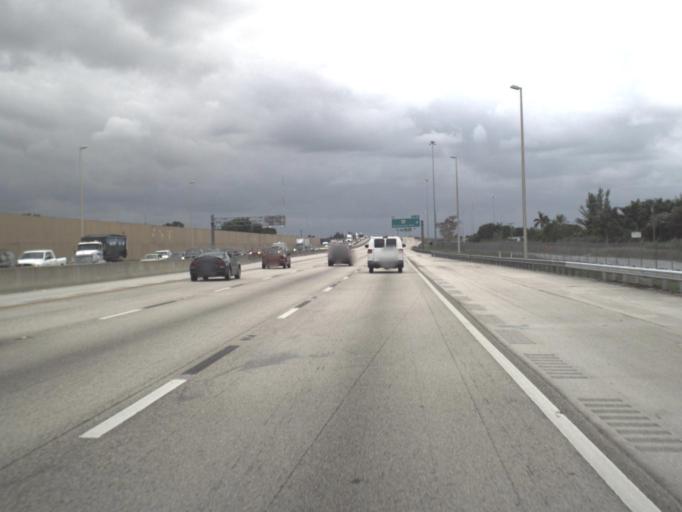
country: US
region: Florida
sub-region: Palm Beach County
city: Villages of Oriole
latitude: 26.5362
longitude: -80.1728
